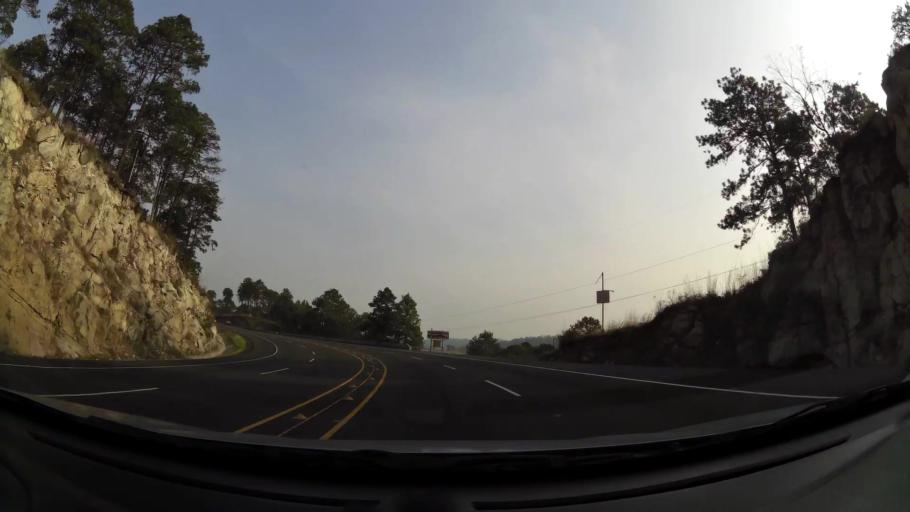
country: HN
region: Francisco Morazan
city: Zambrano
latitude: 14.2505
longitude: -87.3757
